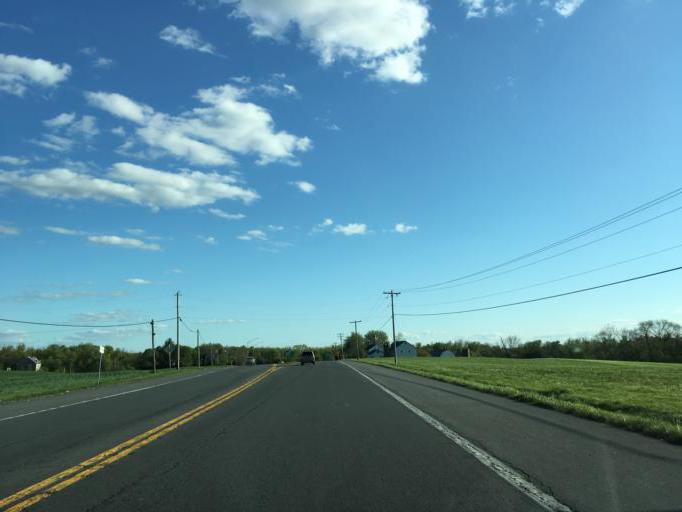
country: US
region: Maryland
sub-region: Frederick County
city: Walkersville
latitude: 39.4580
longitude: -77.3663
